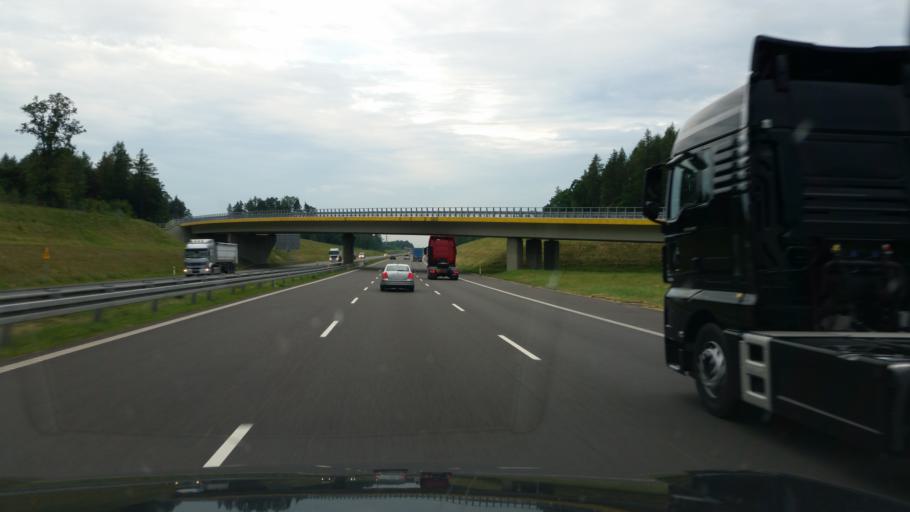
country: PL
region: Silesian Voivodeship
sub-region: Powiat rybnicki
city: Stanowice
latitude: 50.1193
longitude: 18.6843
